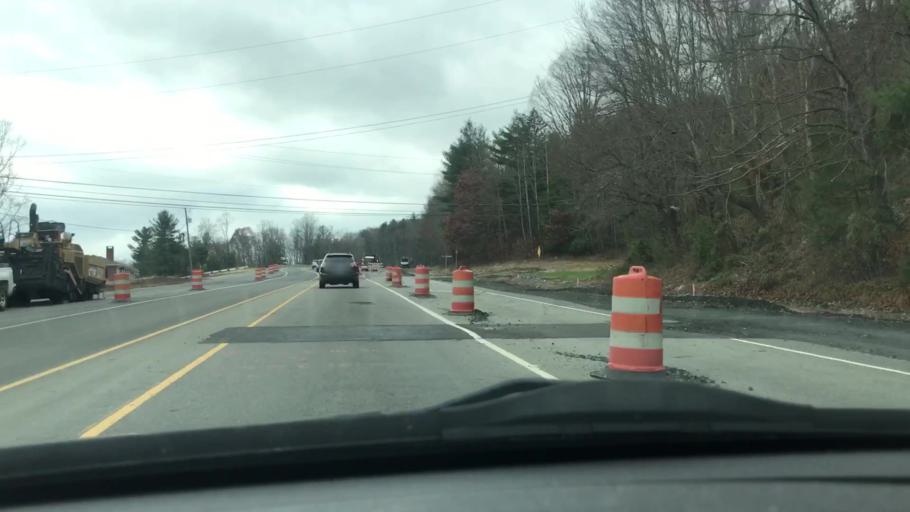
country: US
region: North Carolina
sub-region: Mitchell County
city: Spruce Pine
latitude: 35.9129
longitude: -82.0927
